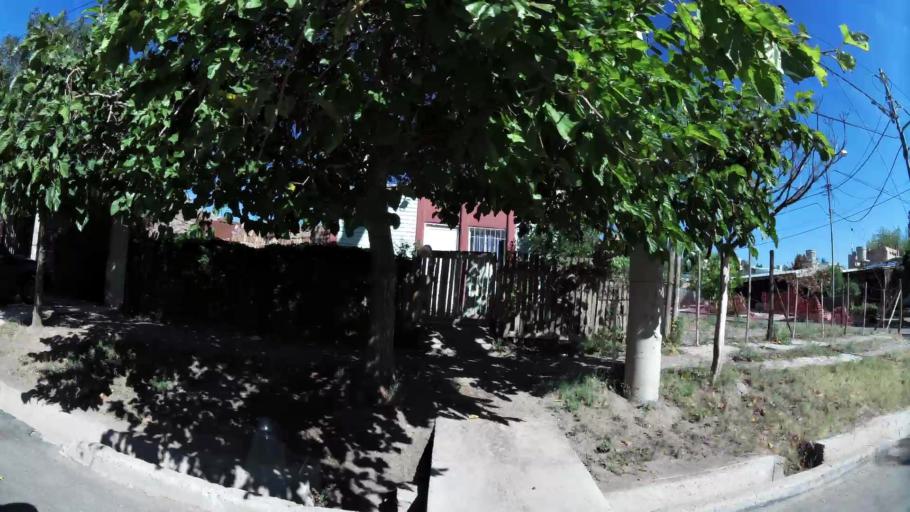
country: AR
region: Mendoza
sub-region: Departamento de Godoy Cruz
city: Godoy Cruz
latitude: -32.9049
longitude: -68.8825
